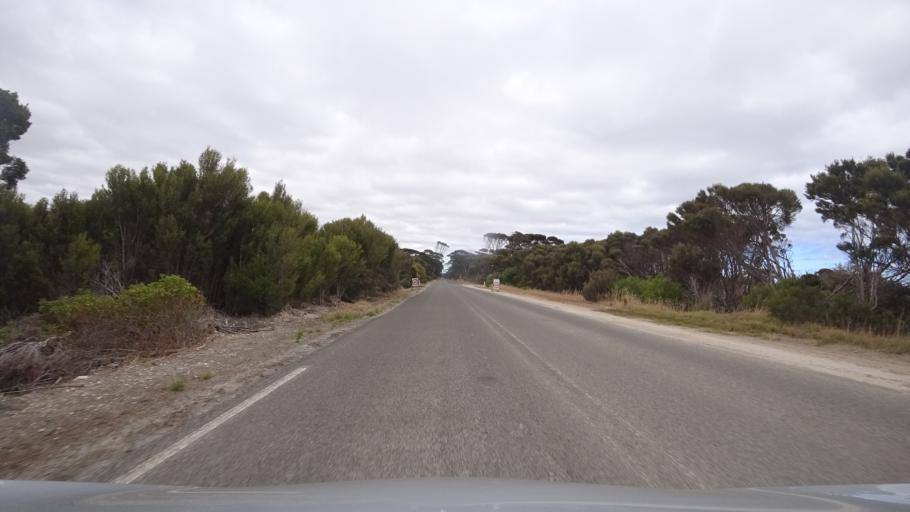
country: AU
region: South Australia
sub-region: Kangaroo Island
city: Kingscote
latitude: -35.6255
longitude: 137.5371
